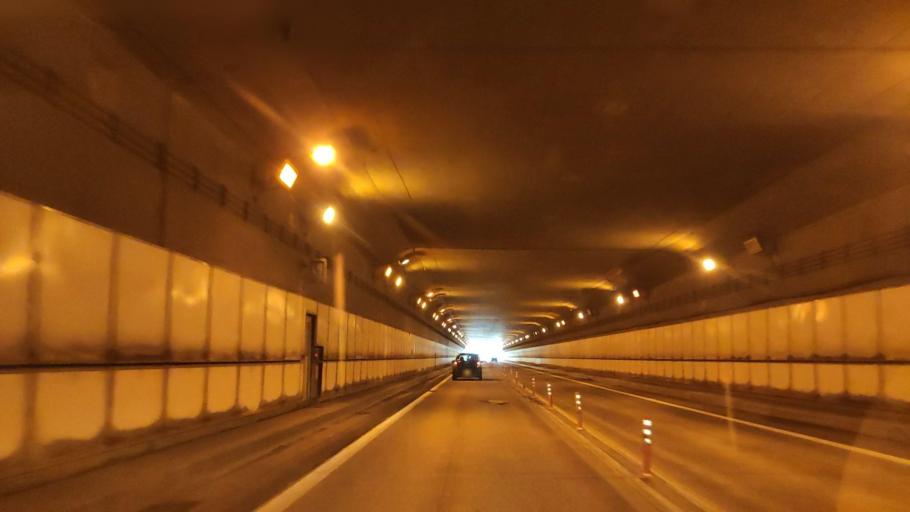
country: JP
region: Akita
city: Odate
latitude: 40.2755
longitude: 140.5342
